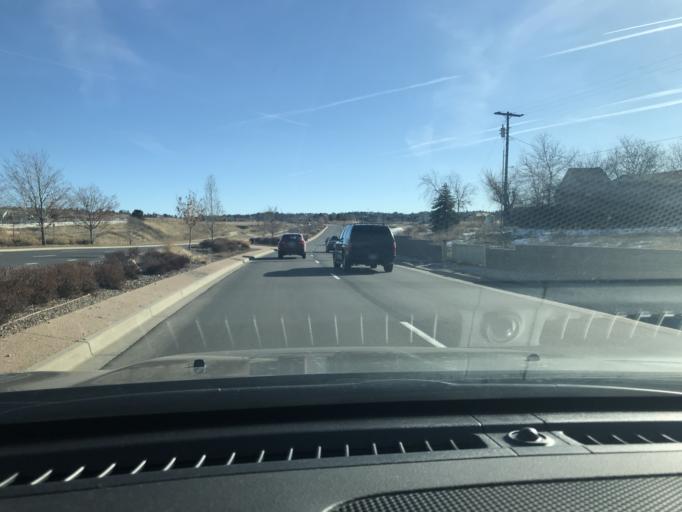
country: US
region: Colorado
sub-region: Douglas County
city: Parker
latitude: 39.5372
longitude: -104.7645
